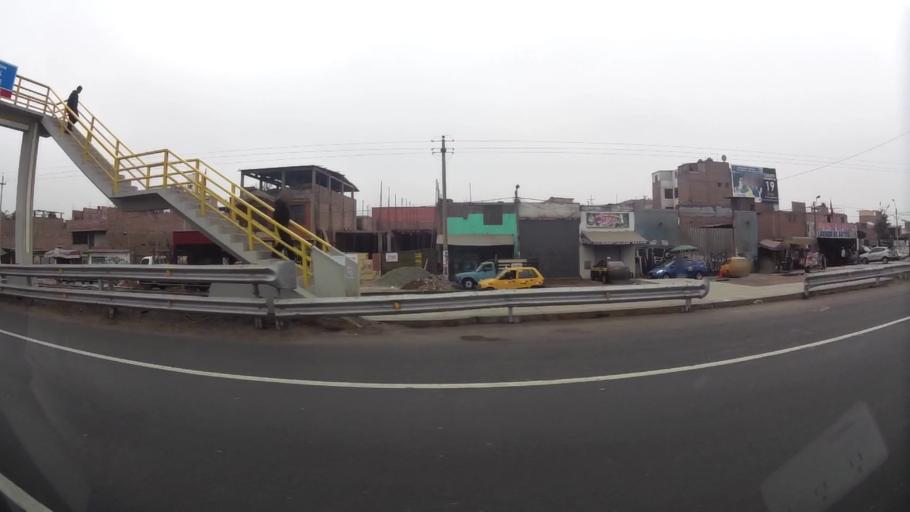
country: PE
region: Lima
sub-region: Lima
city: Surco
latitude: -12.1590
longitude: -76.9828
